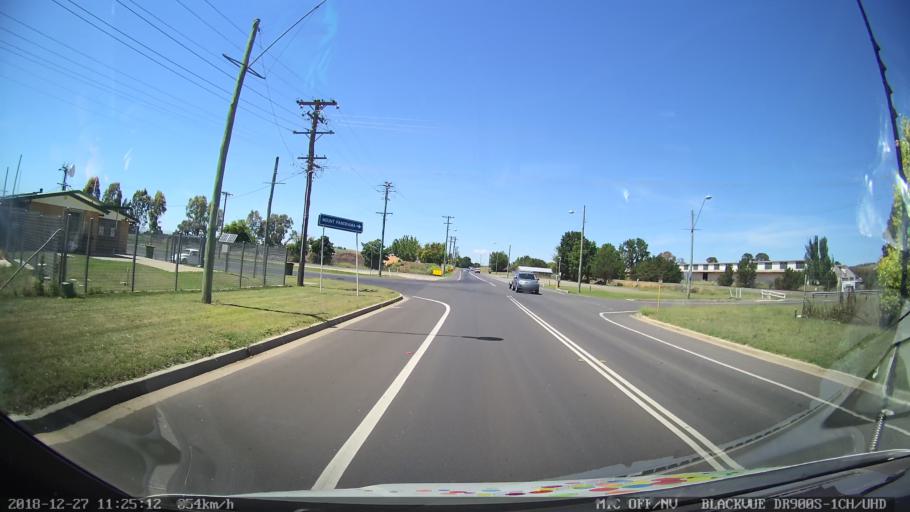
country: AU
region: New South Wales
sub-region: Bathurst Regional
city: Bathurst
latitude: -33.4397
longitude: 149.5786
